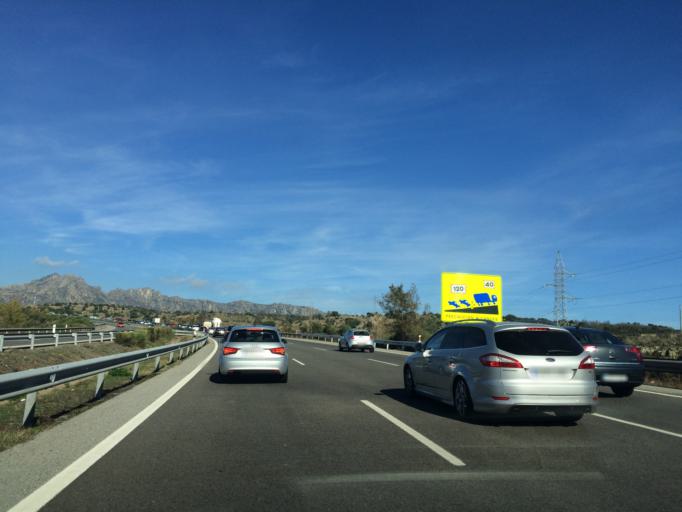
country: ES
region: Madrid
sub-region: Provincia de Madrid
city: Cabanillas de la Sierra
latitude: 40.8297
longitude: -3.6143
